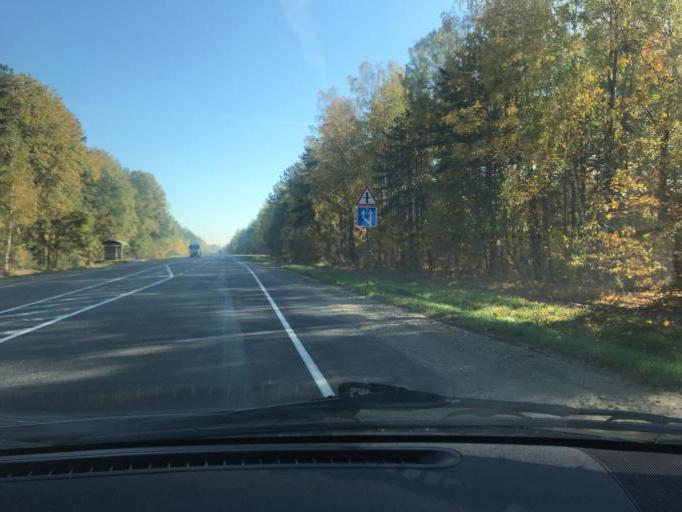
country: BY
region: Brest
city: Ivanava
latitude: 52.1543
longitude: 25.5984
